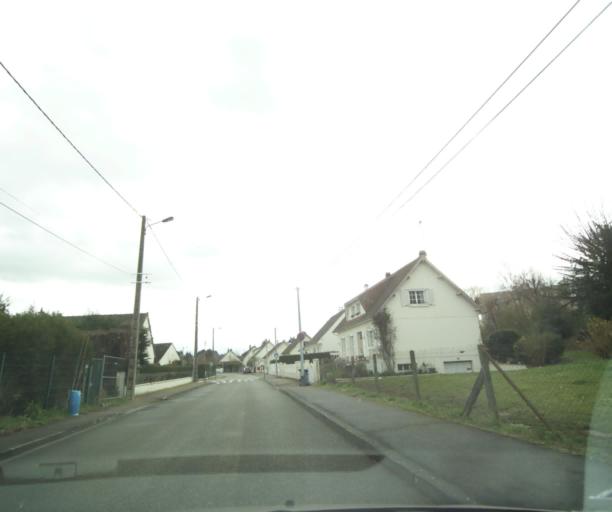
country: FR
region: Picardie
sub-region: Departement de l'Oise
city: Noyon
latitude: 49.5838
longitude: 2.9882
